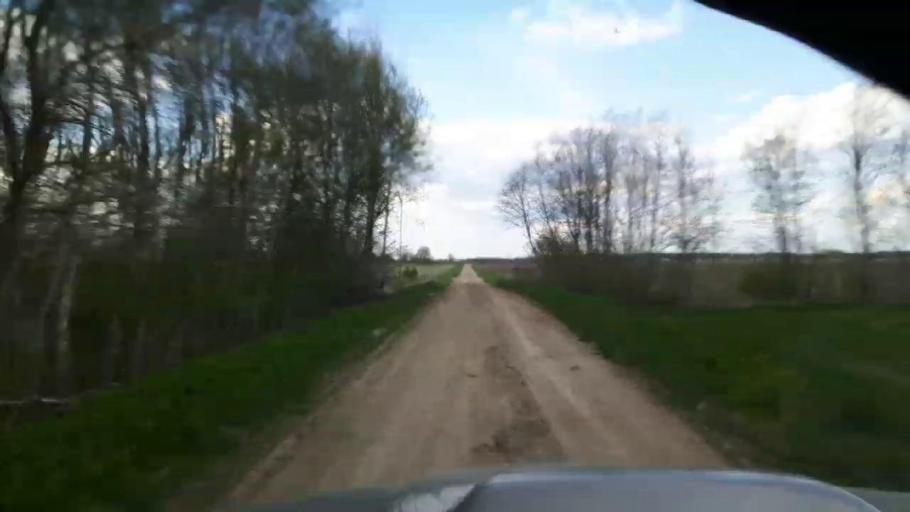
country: EE
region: Paernumaa
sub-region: Sindi linn
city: Sindi
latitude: 58.4321
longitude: 24.7709
